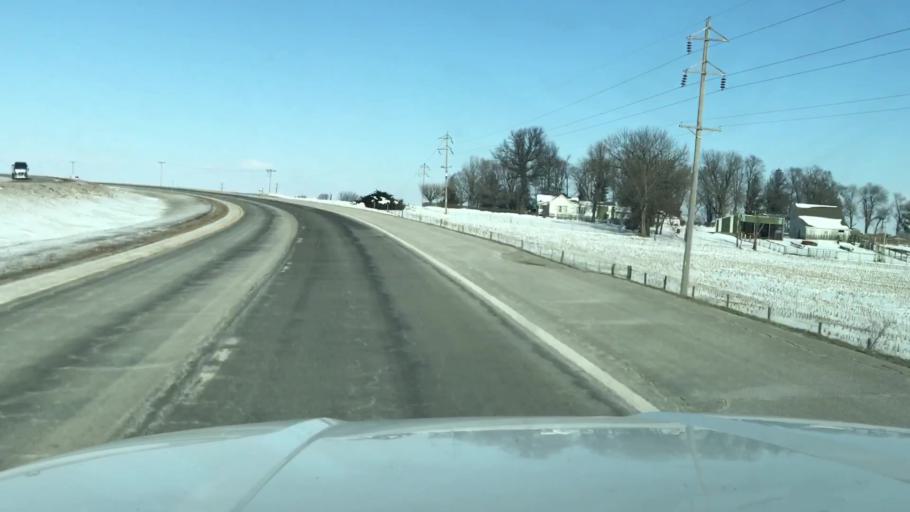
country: US
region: Missouri
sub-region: Nodaway County
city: Maryville
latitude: 40.2709
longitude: -94.8665
